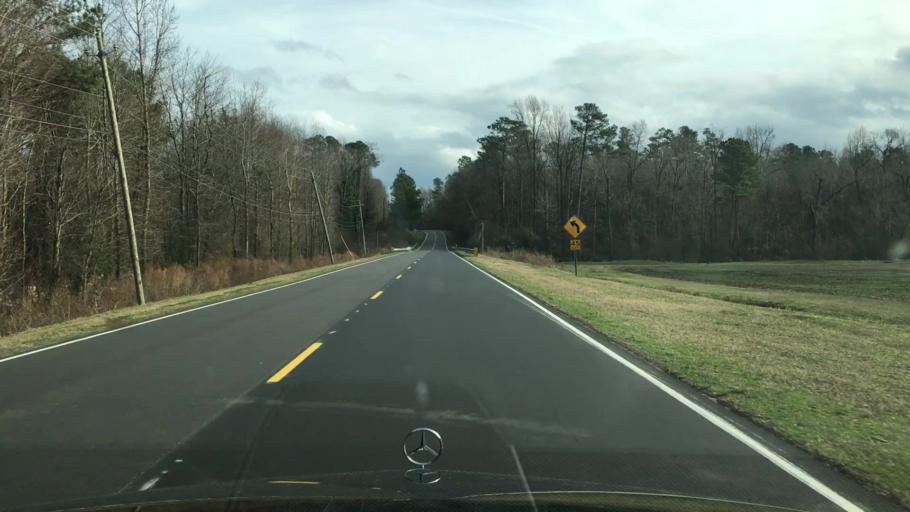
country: US
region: North Carolina
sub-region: Duplin County
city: Kenansville
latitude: 34.9633
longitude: -77.9964
